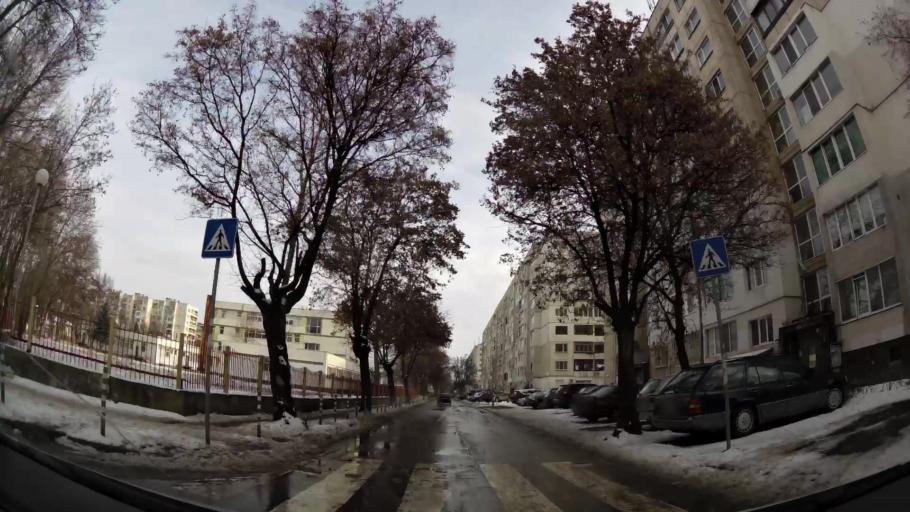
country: BG
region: Sofia-Capital
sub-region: Stolichna Obshtina
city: Sofia
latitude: 42.7060
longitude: 23.3443
